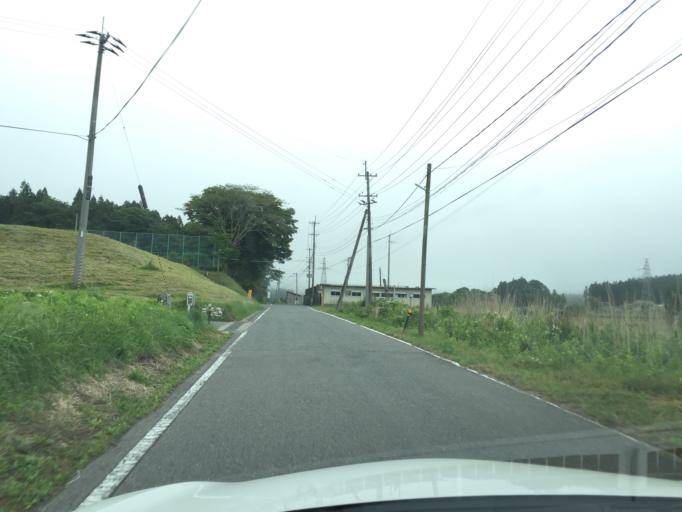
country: JP
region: Fukushima
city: Funehikimachi-funehiki
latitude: 37.2988
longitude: 140.7064
